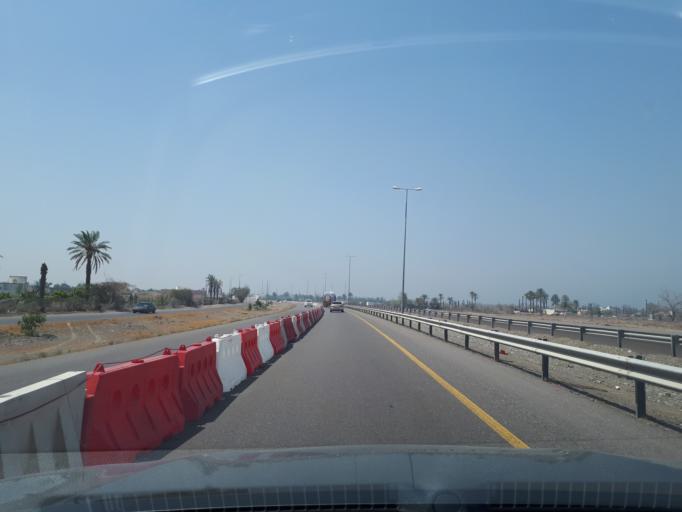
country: OM
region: Al Batinah
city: Al Liwa'
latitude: 24.5974
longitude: 56.5302
